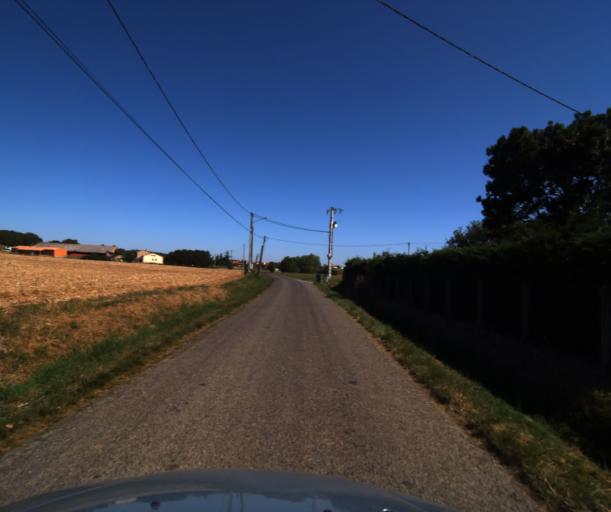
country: FR
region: Midi-Pyrenees
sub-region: Departement de la Haute-Garonne
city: Eaunes
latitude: 43.4154
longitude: 1.3535
